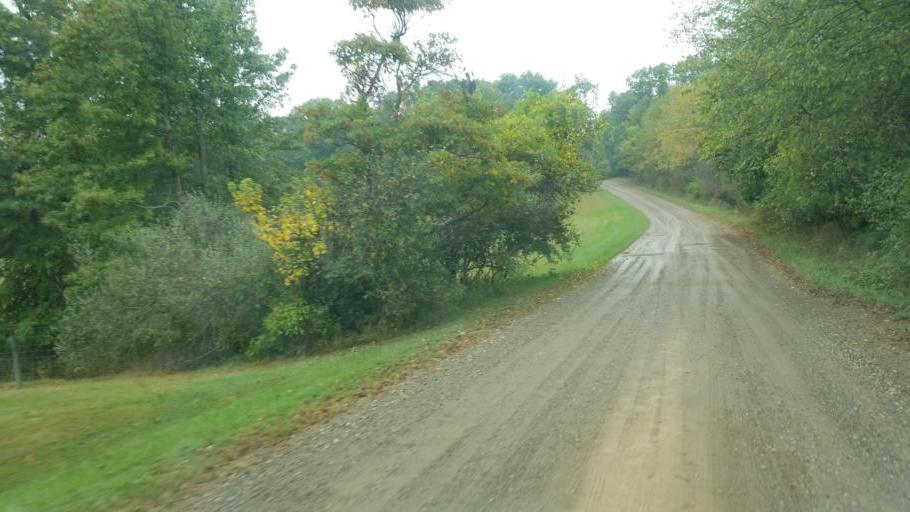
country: US
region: Ohio
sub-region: Ashland County
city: Loudonville
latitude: 40.5754
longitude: -82.2762
